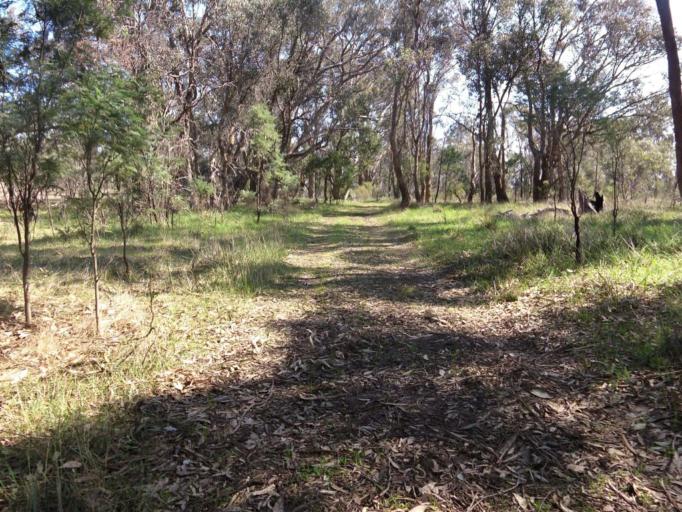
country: AU
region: Victoria
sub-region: Murrindindi
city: Alexandra
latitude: -36.9783
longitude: 145.7093
